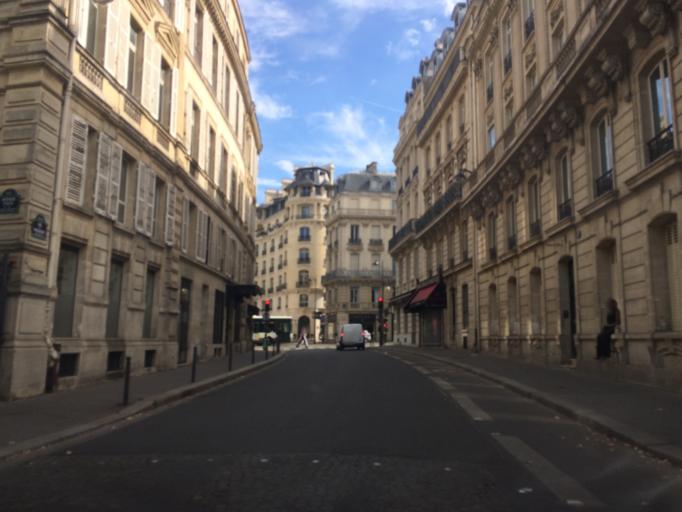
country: FR
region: Ile-de-France
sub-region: Departement des Hauts-de-Seine
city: Levallois-Perret
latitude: 48.8735
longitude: 2.2928
